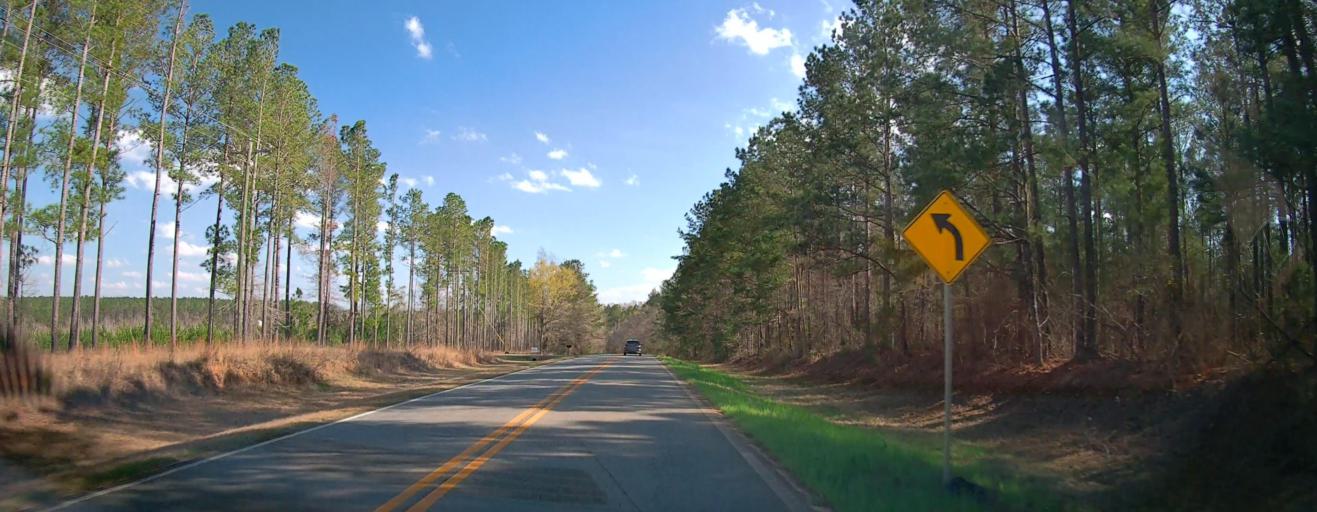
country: US
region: Georgia
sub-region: Laurens County
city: Dublin
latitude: 32.5773
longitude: -83.0493
